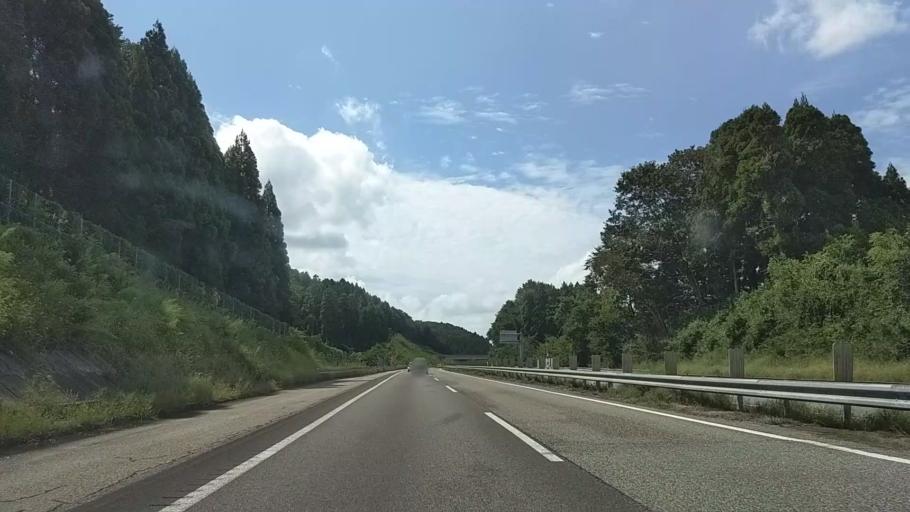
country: JP
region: Toyama
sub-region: Oyabe Shi
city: Oyabe
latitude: 36.6271
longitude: 136.8377
